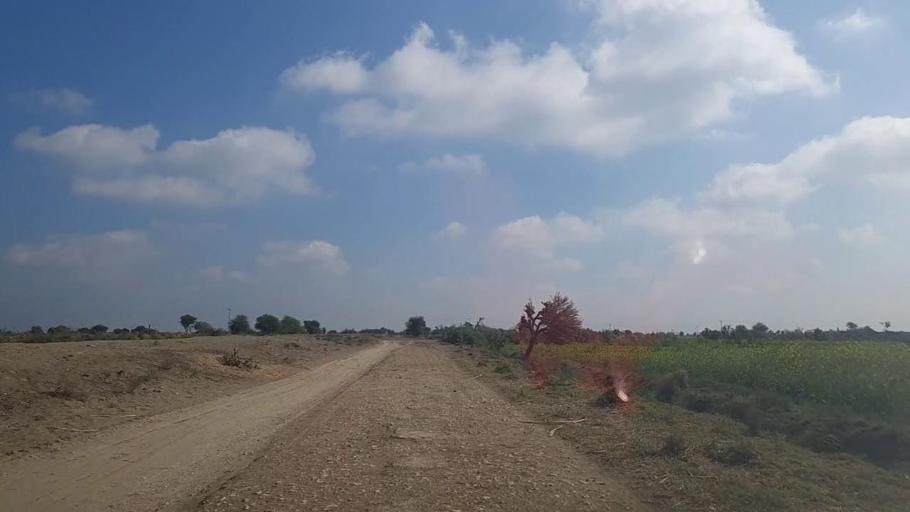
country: PK
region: Sindh
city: Sanghar
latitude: 26.0539
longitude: 68.9723
